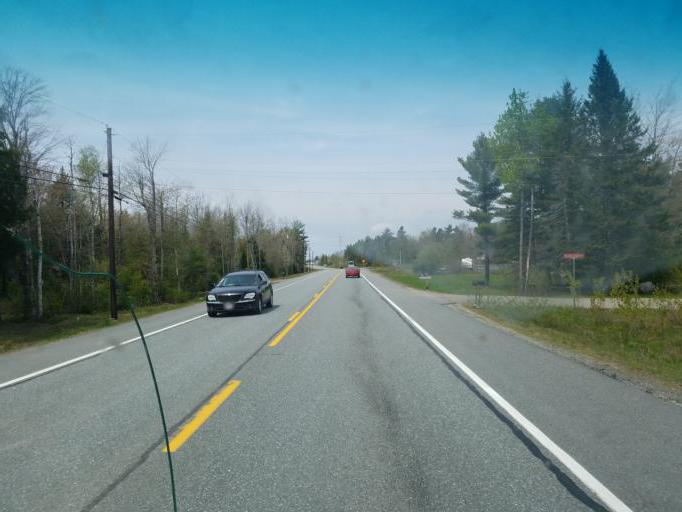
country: US
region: Maine
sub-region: Hancock County
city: Surry
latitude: 44.6104
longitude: -68.5205
